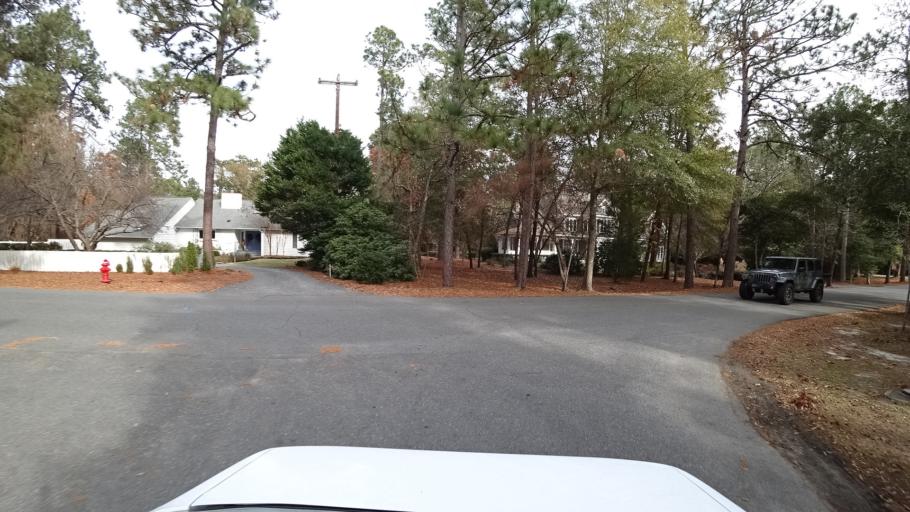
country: US
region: North Carolina
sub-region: Moore County
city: Pinehurst
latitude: 35.2009
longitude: -79.4593
